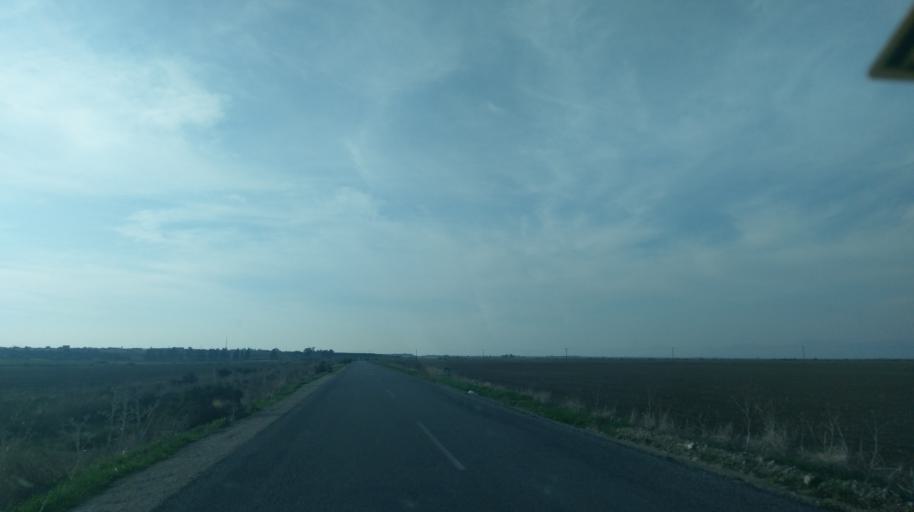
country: CY
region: Ammochostos
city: Acheritou
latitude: 35.0955
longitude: 33.8220
